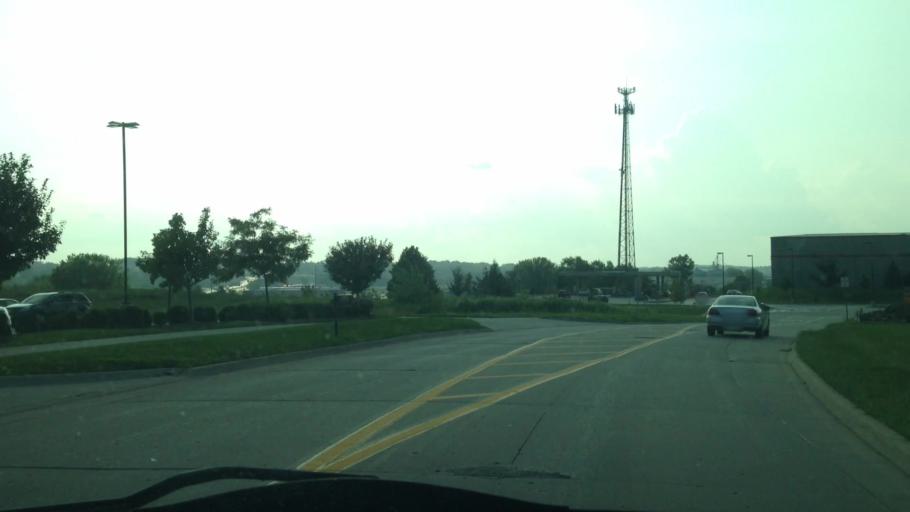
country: US
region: Iowa
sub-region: Johnson County
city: Coralville
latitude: 41.6955
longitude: -91.6158
